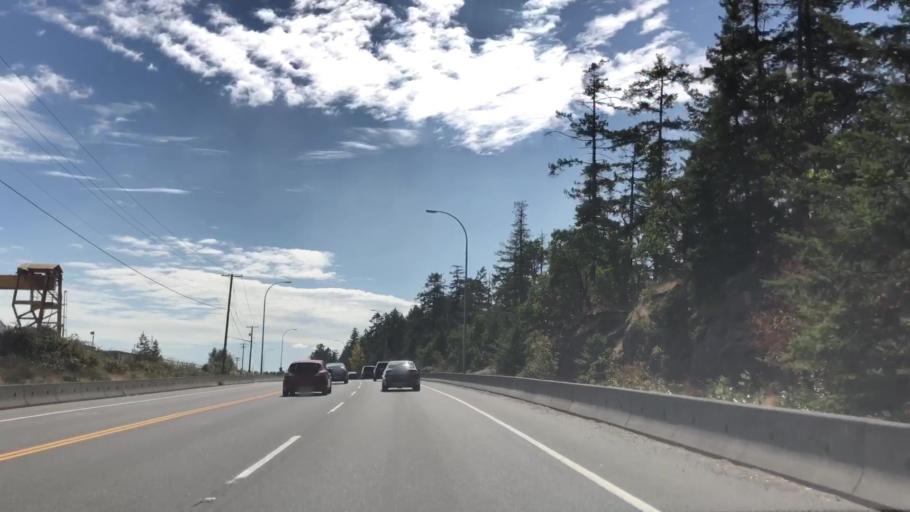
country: CA
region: British Columbia
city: Nanaimo
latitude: 49.1463
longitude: -123.8860
